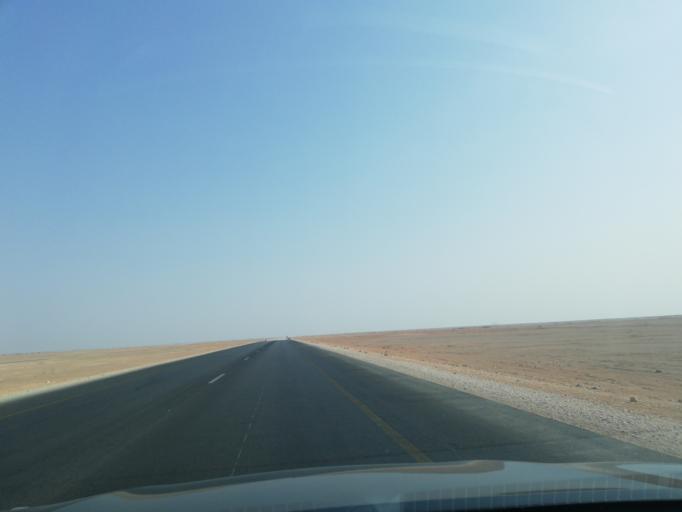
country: OM
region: Zufar
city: Salalah
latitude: 17.8759
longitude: 54.0077
